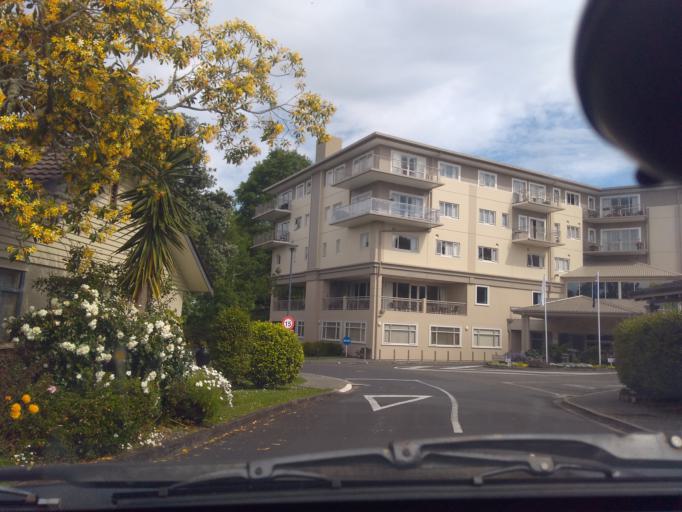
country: NZ
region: Auckland
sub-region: Auckland
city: Titirangi
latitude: -36.9367
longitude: 174.6725
